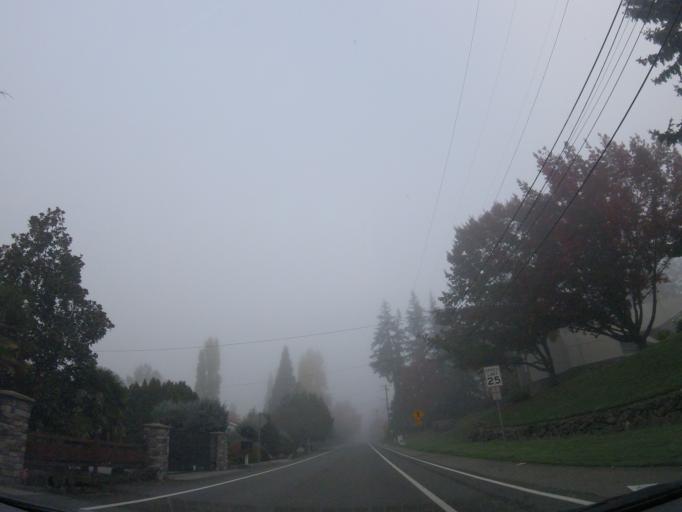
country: US
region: Washington
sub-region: King County
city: Bellevue
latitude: 47.6275
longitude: -122.1962
